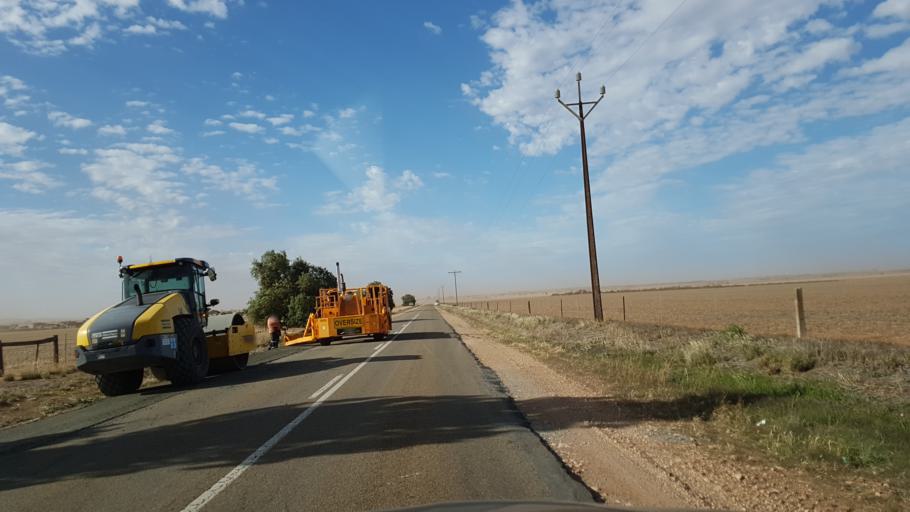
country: AU
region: South Australia
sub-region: Clare and Gilbert Valleys
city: Clare
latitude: -33.8823
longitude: 138.4795
